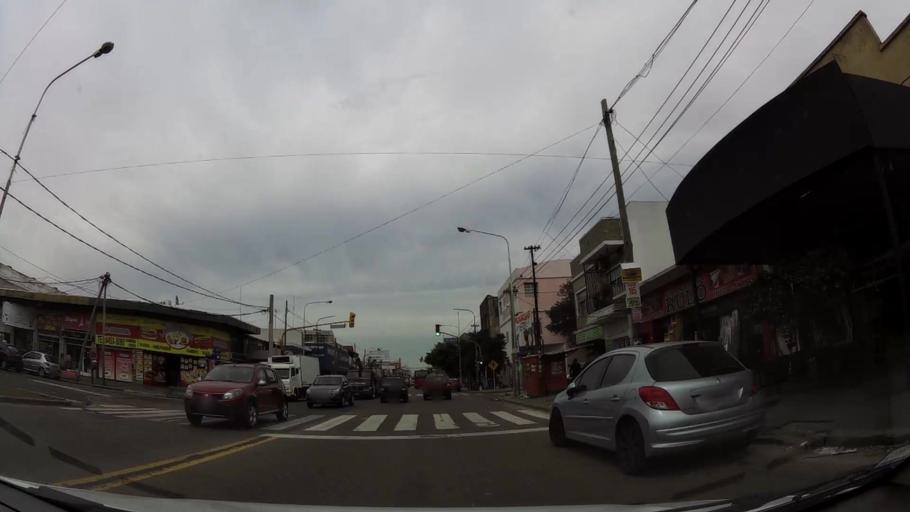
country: AR
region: Buenos Aires F.D.
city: Villa Lugano
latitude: -34.6815
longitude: -58.5134
